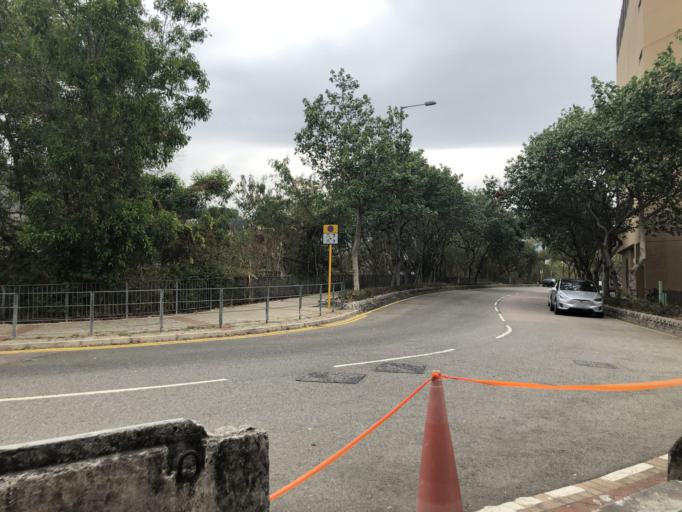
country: HK
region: Sai Kung
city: Sai Kung
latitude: 22.3854
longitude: 114.2738
